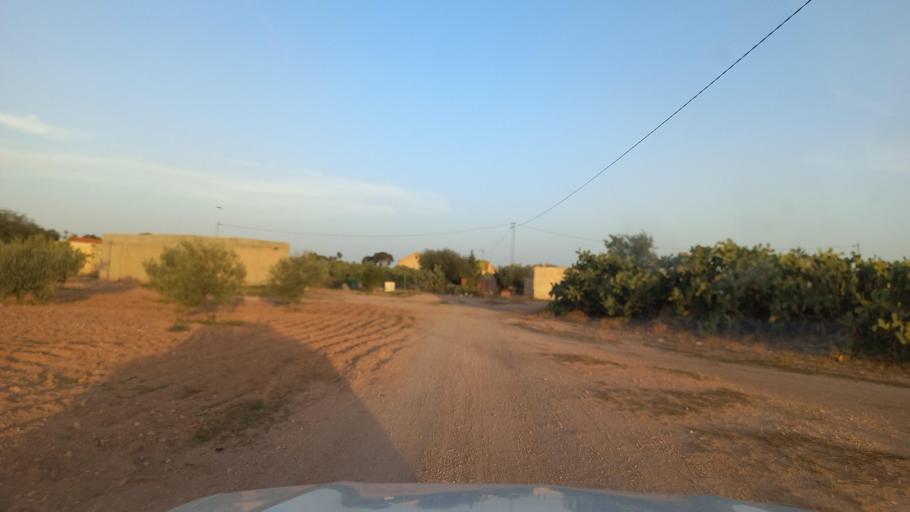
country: TN
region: Al Qasrayn
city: Kasserine
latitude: 35.2399
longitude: 8.9922
